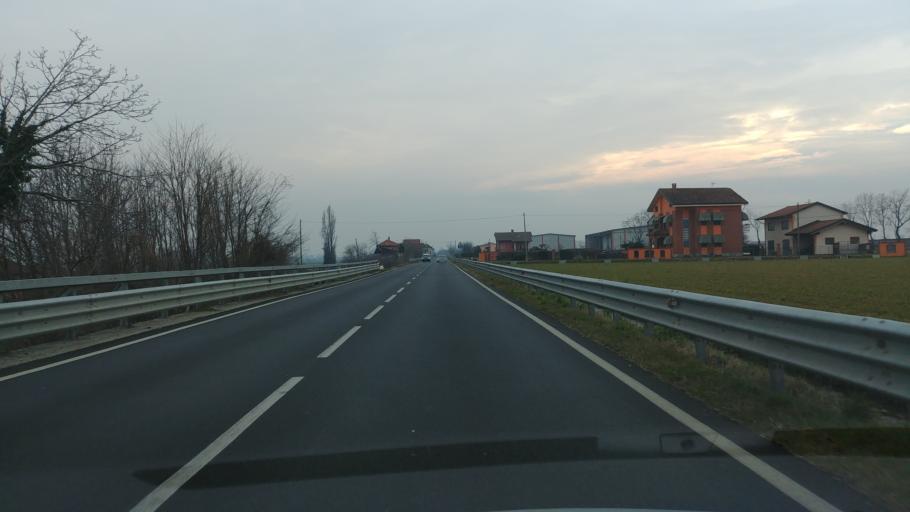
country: IT
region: Piedmont
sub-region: Provincia di Cuneo
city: Montanera
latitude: 44.4790
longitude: 7.6463
